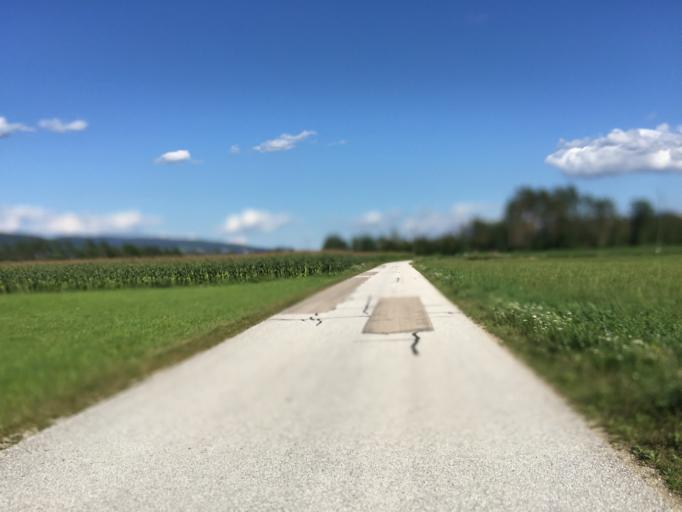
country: AT
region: Carinthia
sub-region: Politischer Bezirk Volkermarkt
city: Feistritz ob Bleiburg
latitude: 46.5651
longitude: 14.7643
